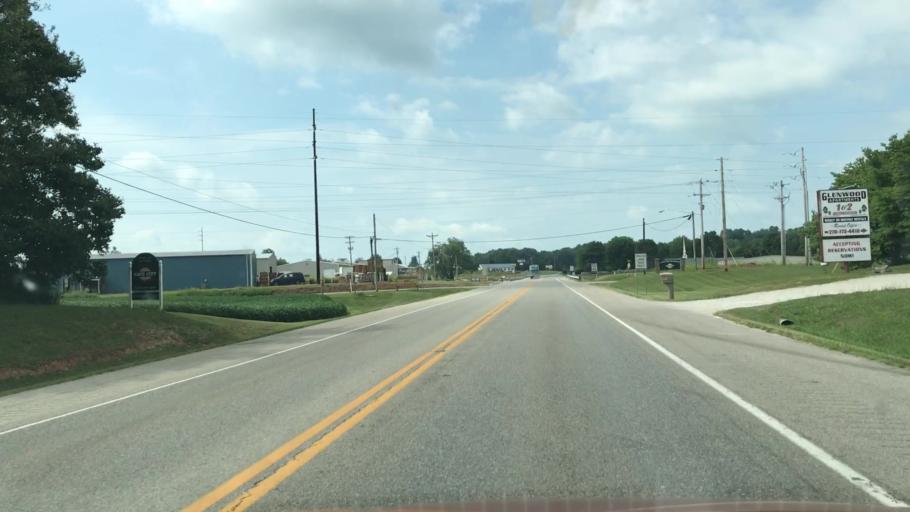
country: US
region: Kentucky
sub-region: Barren County
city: Cave City
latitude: 37.1215
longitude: -85.9621
